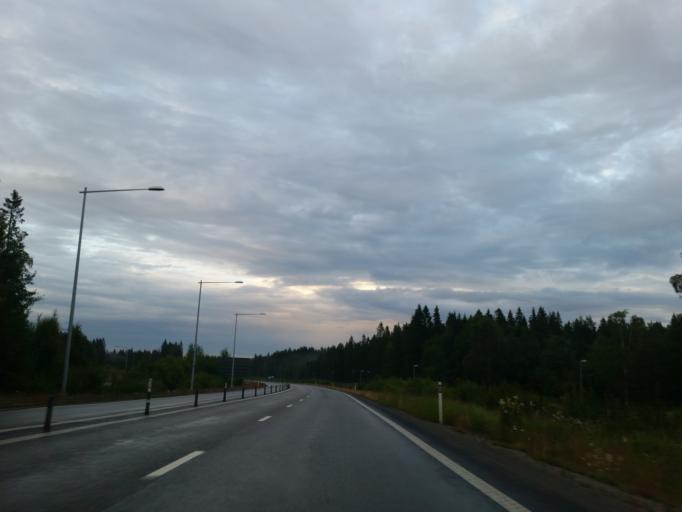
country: SE
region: Vaesterbotten
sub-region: Umea Kommun
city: Ersmark
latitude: 63.8475
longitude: 20.3457
